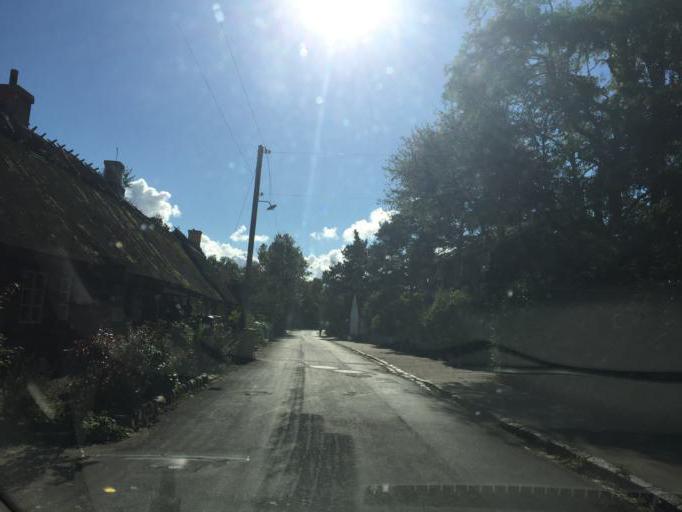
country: DK
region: Zealand
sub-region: Roskilde Kommune
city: Roskilde
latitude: 55.6770
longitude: 12.0873
